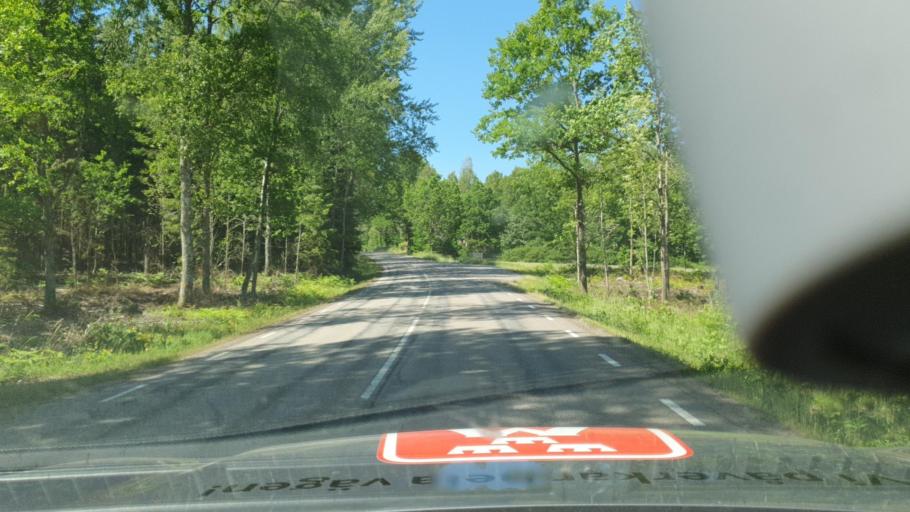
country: SE
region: Kalmar
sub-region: Emmaboda Kommun
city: Emmaboda
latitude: 56.5057
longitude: 15.6655
